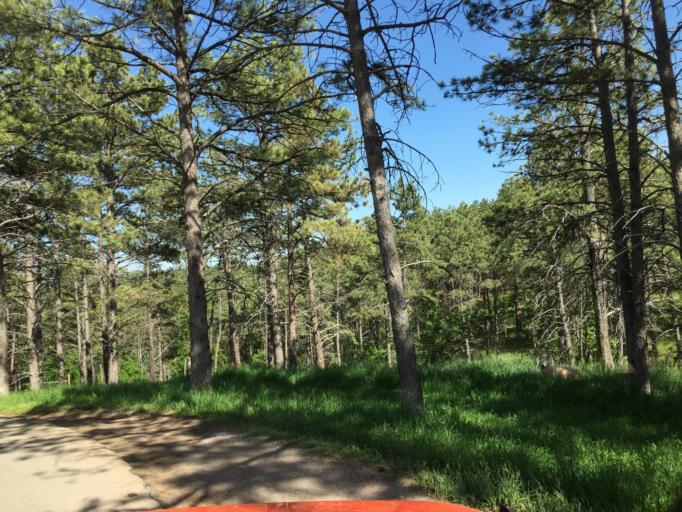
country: US
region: South Dakota
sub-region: Pennington County
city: Colonial Pine Hills
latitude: 43.9789
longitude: -103.2947
